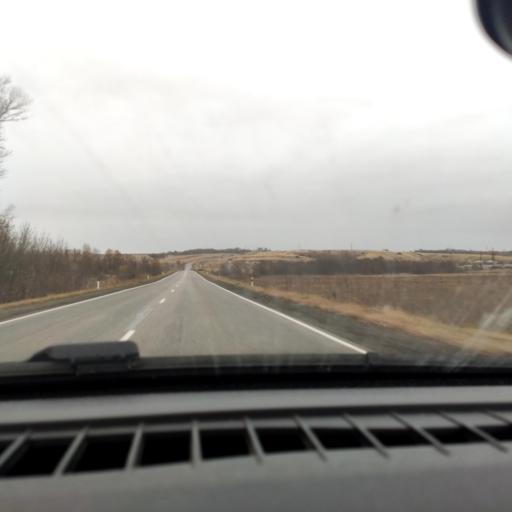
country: RU
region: Voronezj
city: Uryv-Pokrovka
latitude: 51.1276
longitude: 39.0411
